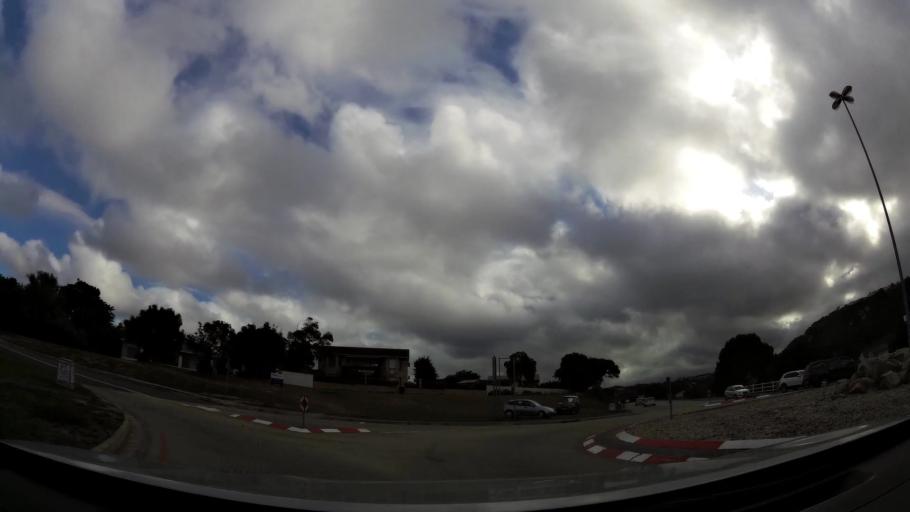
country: ZA
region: Western Cape
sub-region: Eden District Municipality
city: Plettenberg Bay
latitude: -34.0623
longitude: 23.3715
